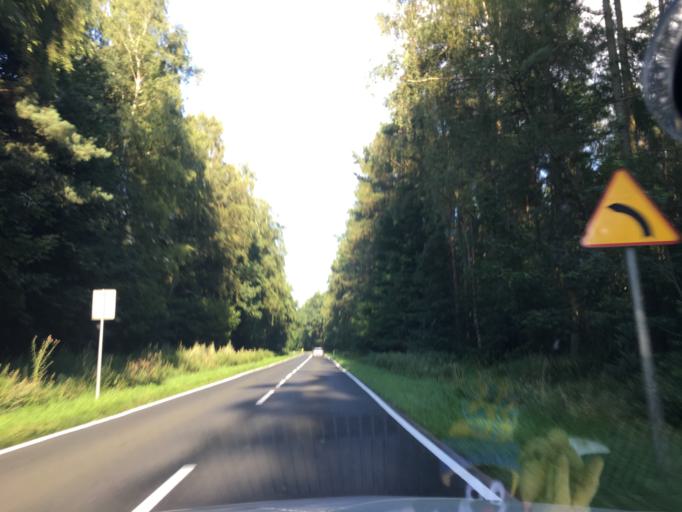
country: PL
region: West Pomeranian Voivodeship
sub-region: Powiat kamienski
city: Dziwnow
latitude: 54.0382
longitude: 14.8463
